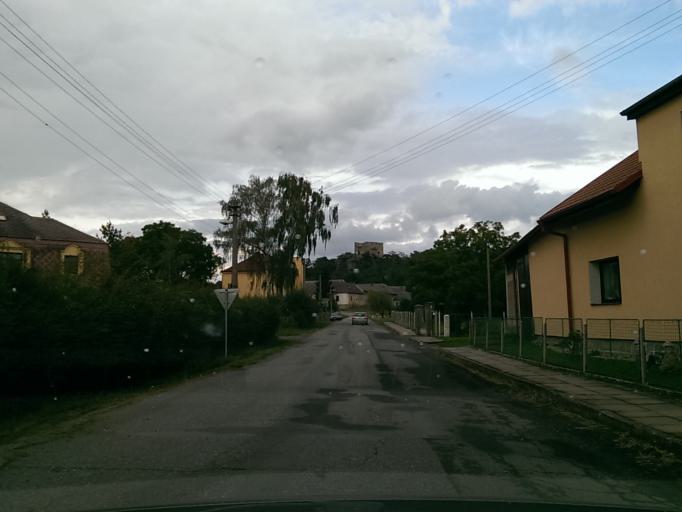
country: CZ
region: Central Bohemia
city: Knezmost
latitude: 50.5066
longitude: 15.0221
